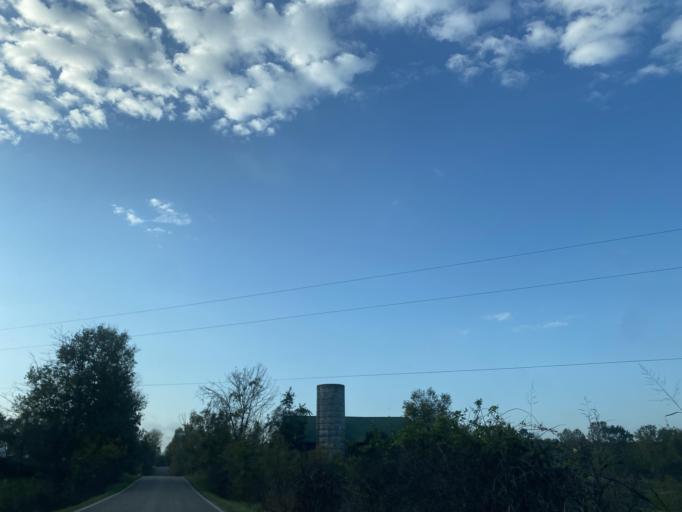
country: US
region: Kentucky
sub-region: Pendleton County
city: Falmouth
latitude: 38.7571
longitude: -84.3395
